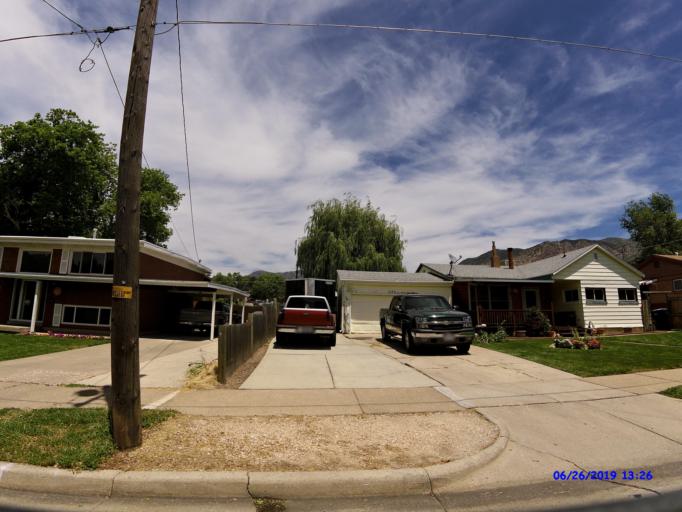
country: US
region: Utah
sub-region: Weber County
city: South Ogden
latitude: 41.2063
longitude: -111.9530
